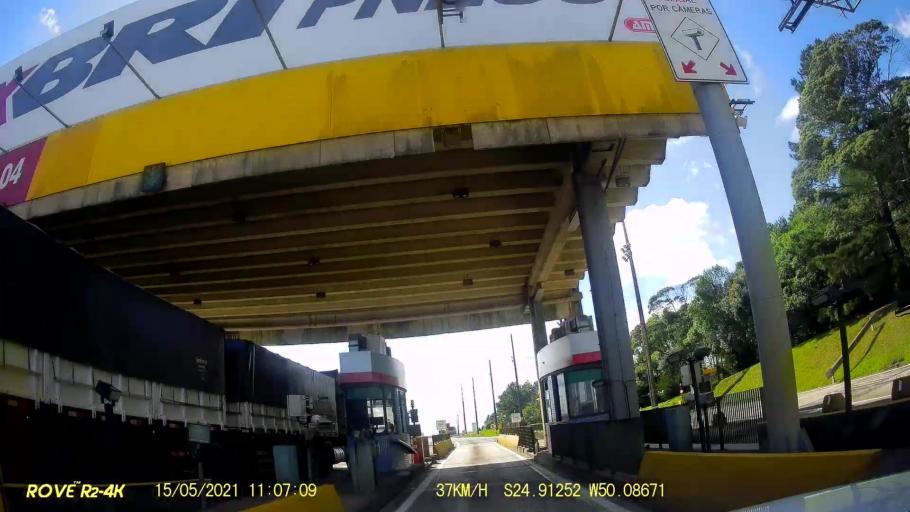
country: BR
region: Parana
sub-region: Carambei
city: Carambei
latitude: -24.9125
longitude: -50.0867
